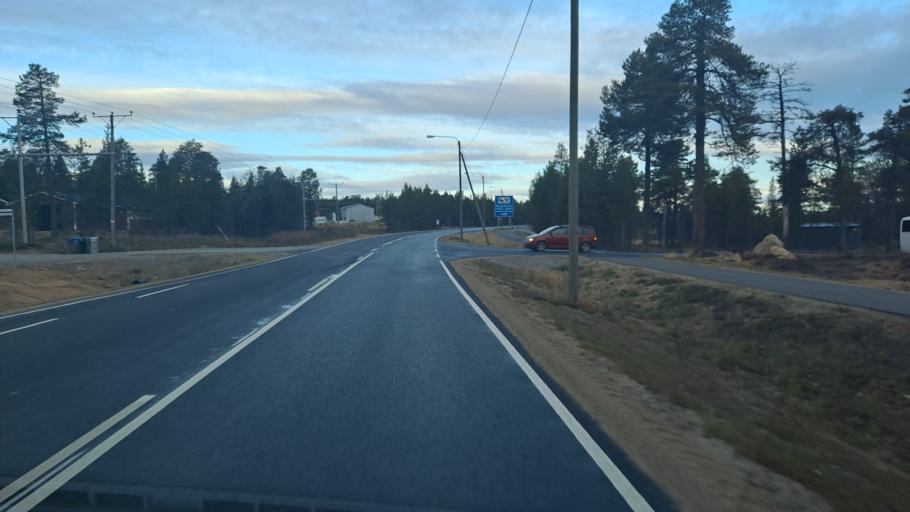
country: FI
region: Lapland
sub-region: Pohjois-Lappi
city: Inari
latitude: 68.8977
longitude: 27.0859
